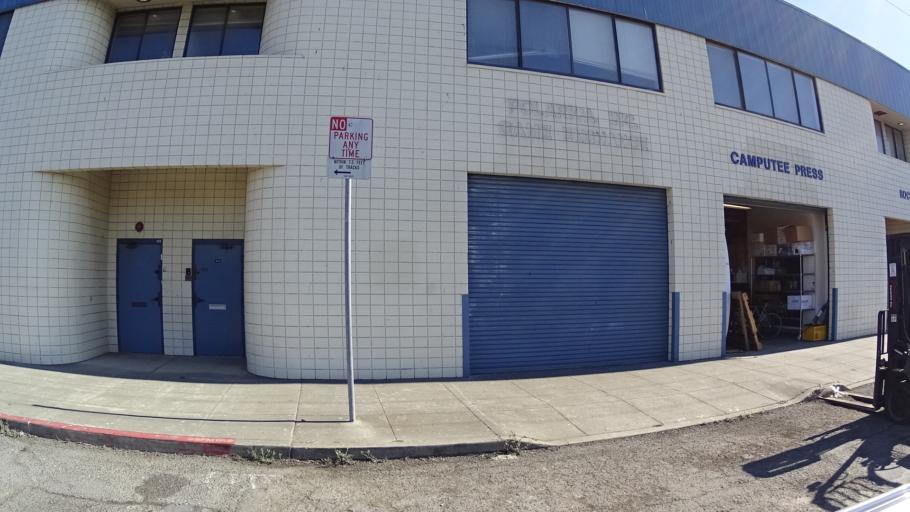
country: US
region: California
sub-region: San Francisco County
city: San Francisco
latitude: 37.7463
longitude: -122.3883
